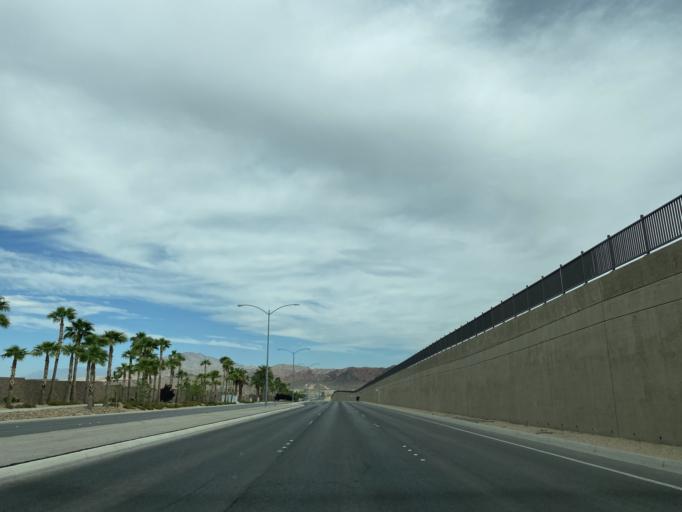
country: US
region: Nevada
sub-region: Clark County
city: Henderson
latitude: 36.0781
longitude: -114.9578
